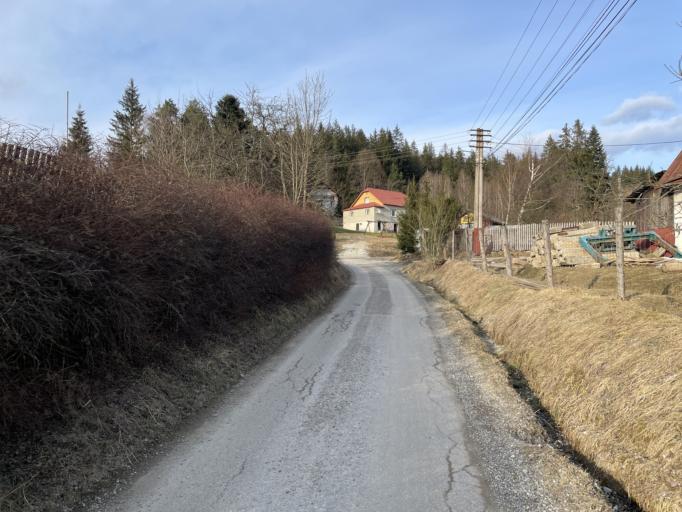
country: CZ
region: Moravskoslezsky
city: Mosty u Jablunkova
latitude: 49.4810
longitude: 18.6941
